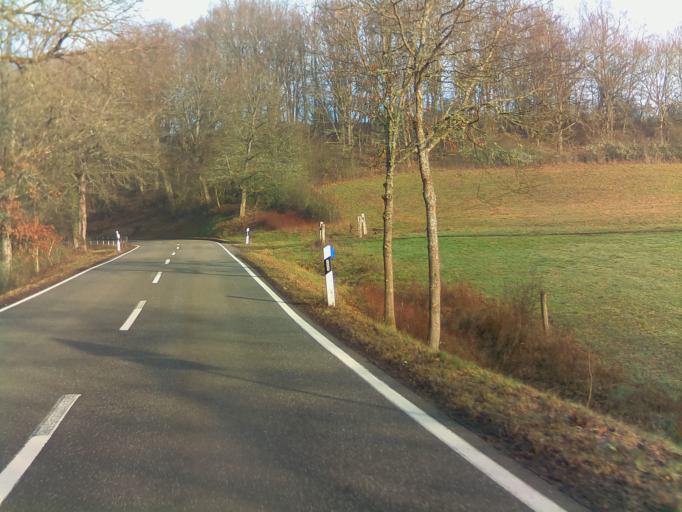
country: DE
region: Rheinland-Pfalz
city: Gries
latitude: 49.4152
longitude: 7.4144
